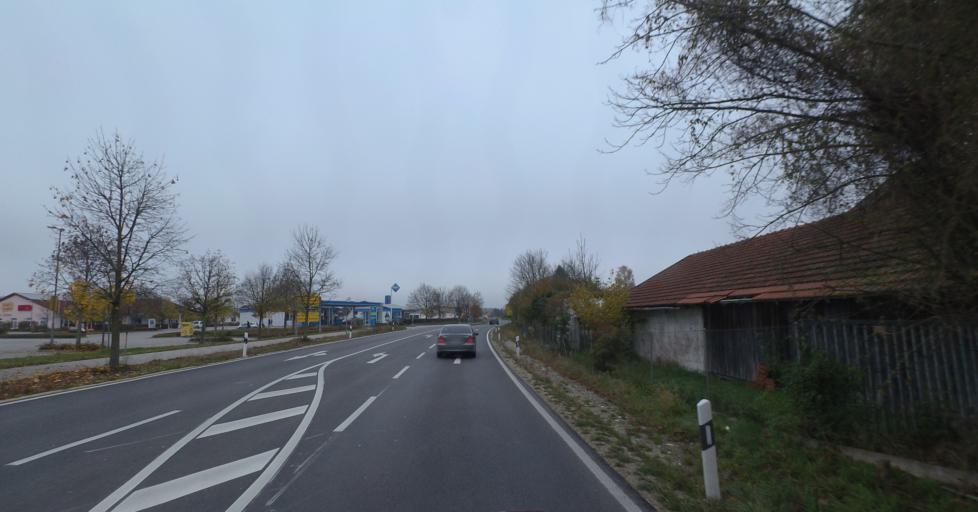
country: DE
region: Bavaria
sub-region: Upper Bavaria
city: Garching an der Alz
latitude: 48.1251
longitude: 12.5748
